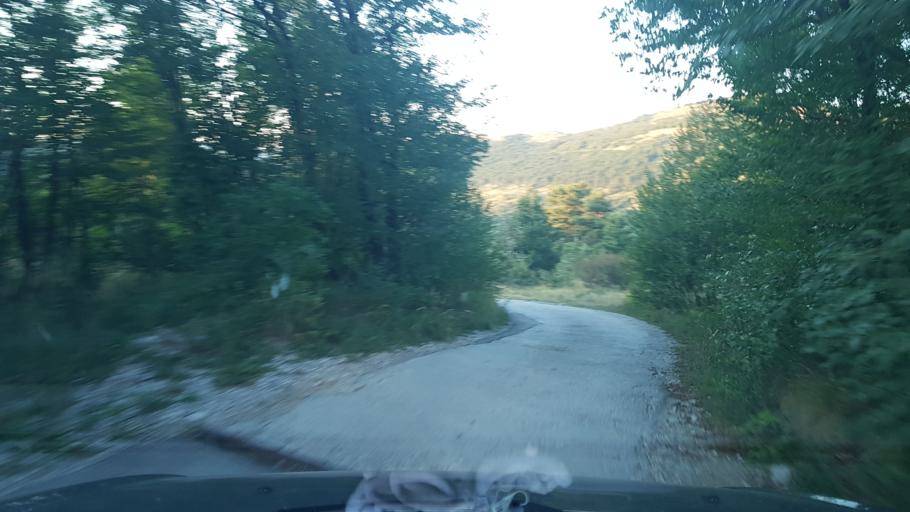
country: SI
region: Vipava
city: Vipava
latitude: 45.7871
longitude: 14.0251
